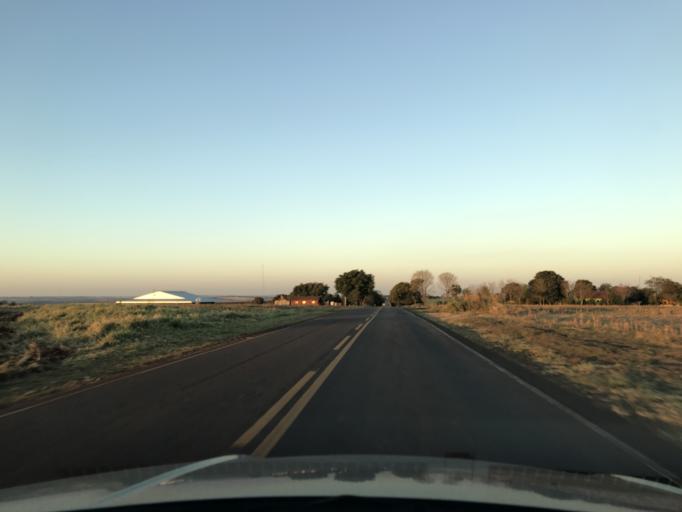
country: BR
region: Parana
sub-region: Palotina
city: Palotina
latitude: -24.2089
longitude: -54.0353
